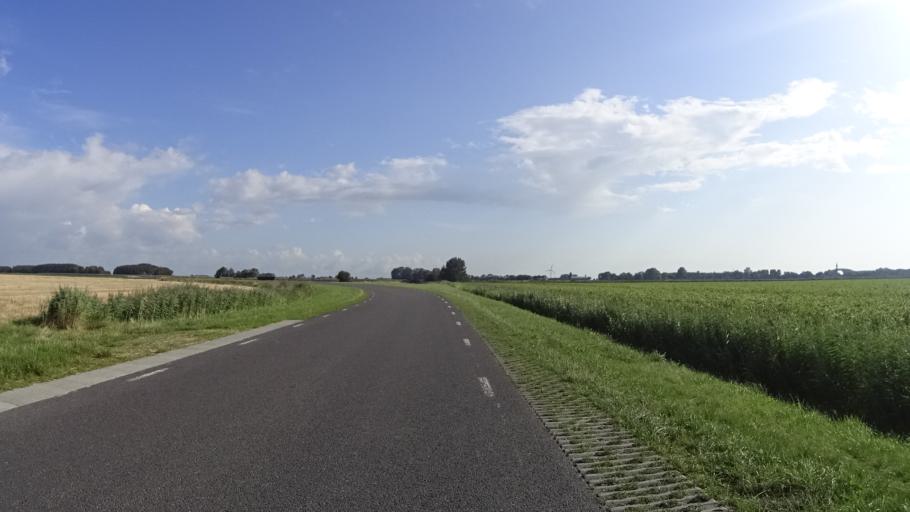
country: NL
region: Friesland
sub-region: Gemeente Harlingen
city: Harlingen
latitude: 53.1265
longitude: 5.4573
